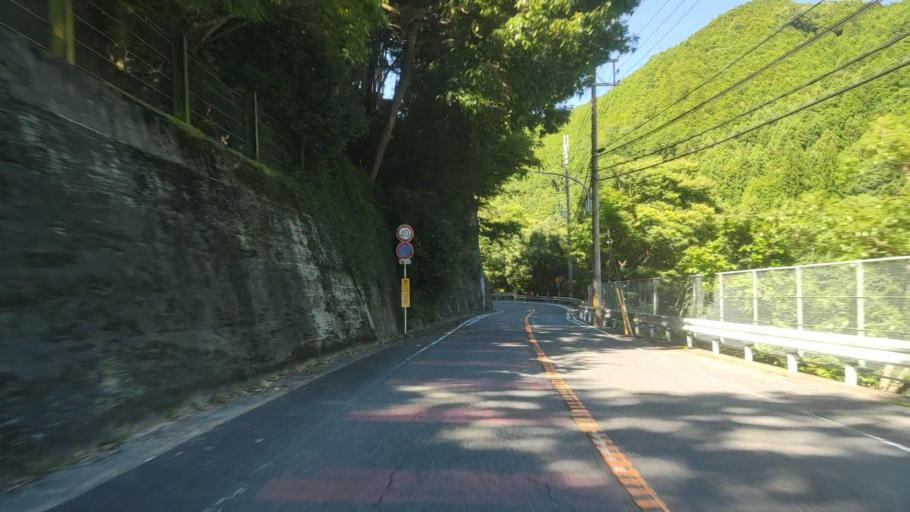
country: JP
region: Nara
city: Yoshino-cho
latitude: 34.3817
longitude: 135.9162
